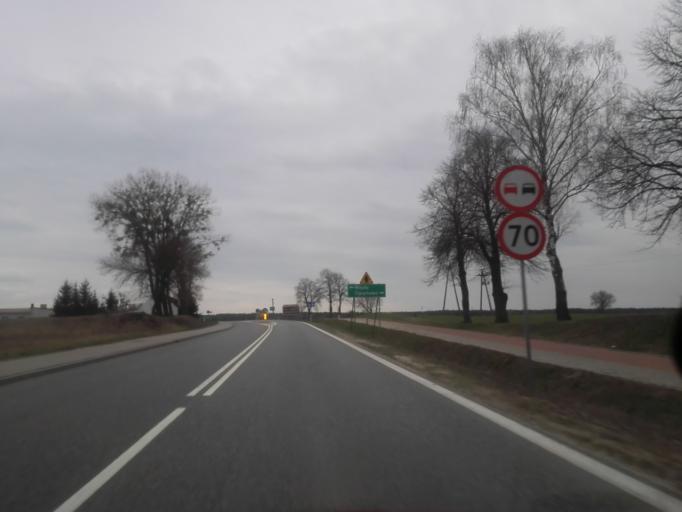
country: PL
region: Podlasie
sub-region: Powiat grajewski
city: Rajgrod
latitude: 53.7254
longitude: 22.6795
